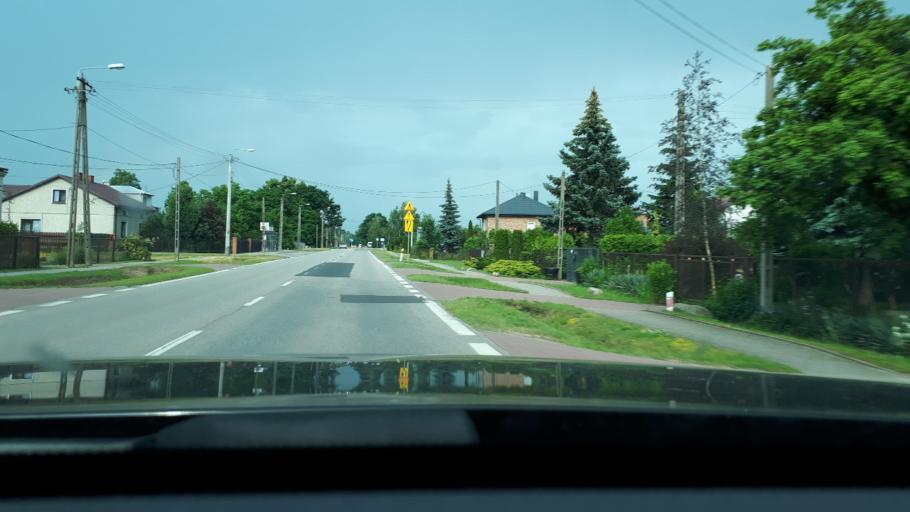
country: PL
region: Masovian Voivodeship
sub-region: Powiat warszawski zachodni
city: Leszno
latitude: 52.2618
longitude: 20.6266
